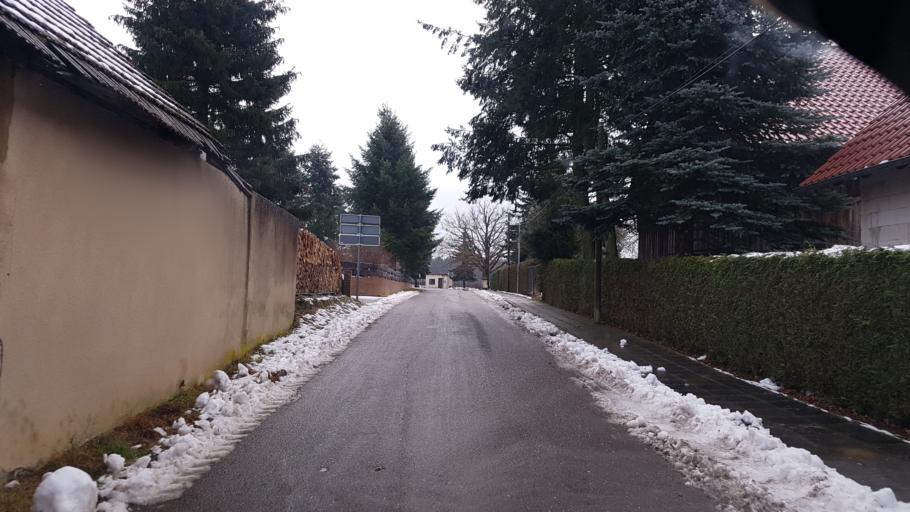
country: DE
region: Brandenburg
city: Straupitz
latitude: 51.9777
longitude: 14.1917
